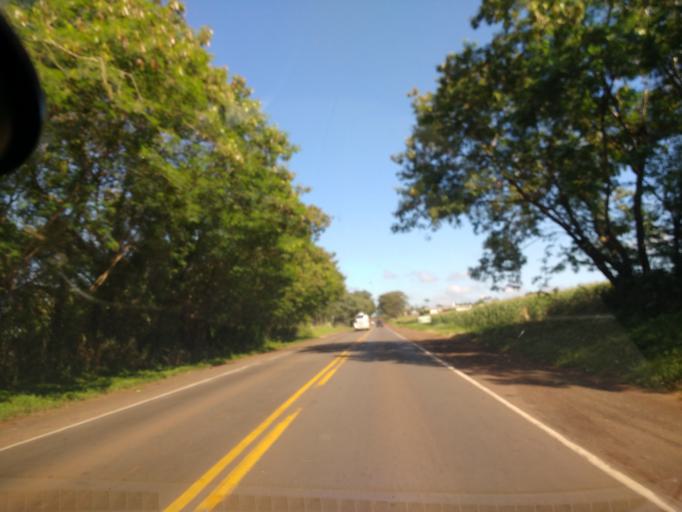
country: BR
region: Parana
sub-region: Terra Boa
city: Terra Boa
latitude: -23.6295
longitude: -52.4555
